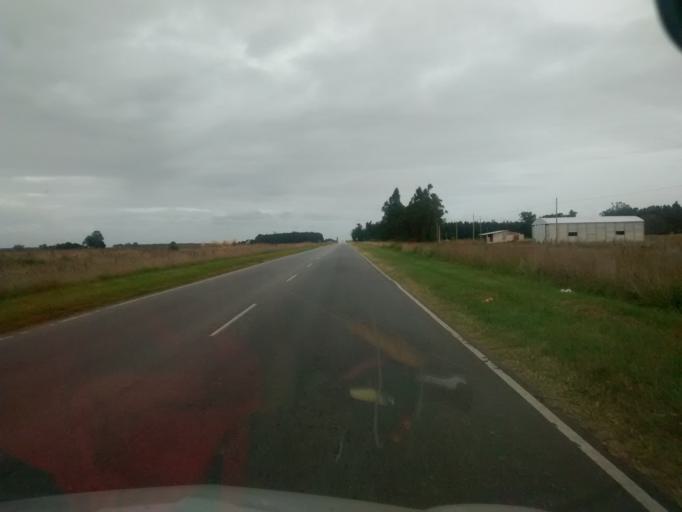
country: AR
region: Buenos Aires
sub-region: Partido de Loberia
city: Loberia
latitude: -38.2086
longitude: -58.7343
